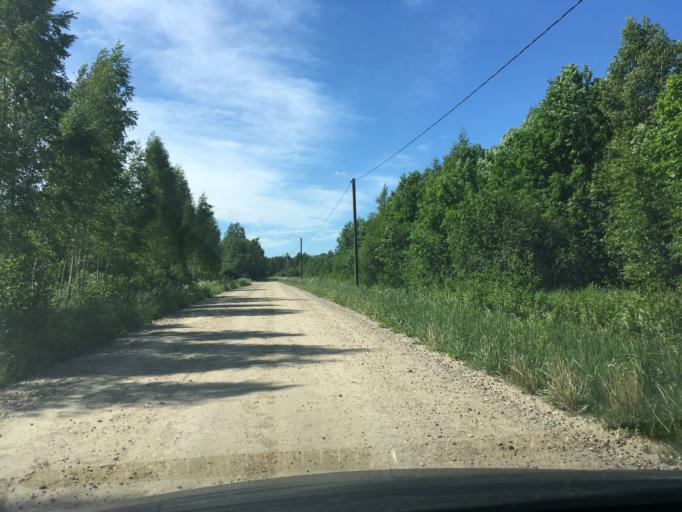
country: EE
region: Paernumaa
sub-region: Audru vald
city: Audru
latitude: 58.4558
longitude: 24.3824
